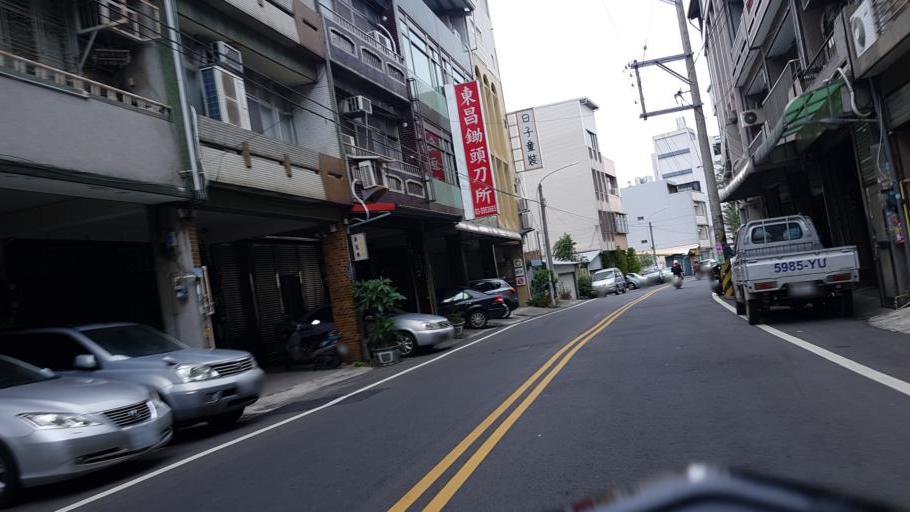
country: TW
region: Taiwan
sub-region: Hsinchu
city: Zhubei
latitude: 24.7339
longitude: 121.0901
